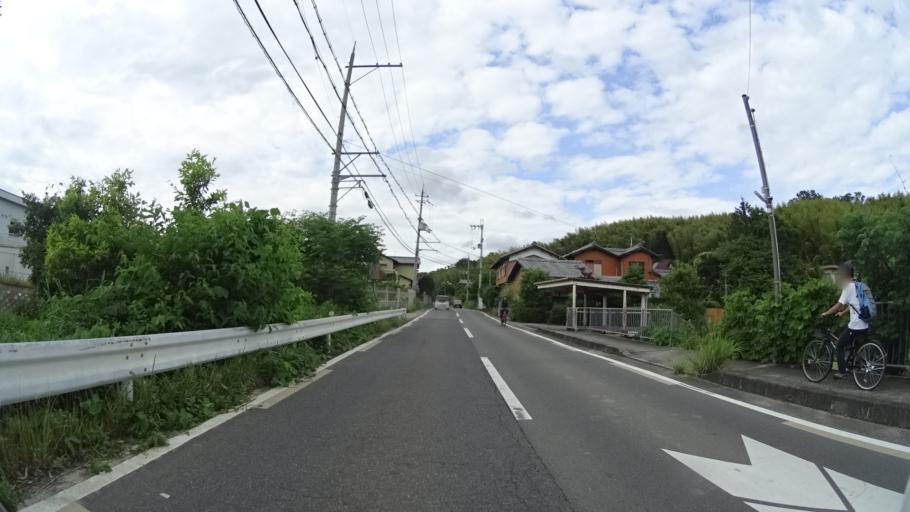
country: JP
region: Nara
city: Nara-shi
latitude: 34.7464
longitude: 135.8360
